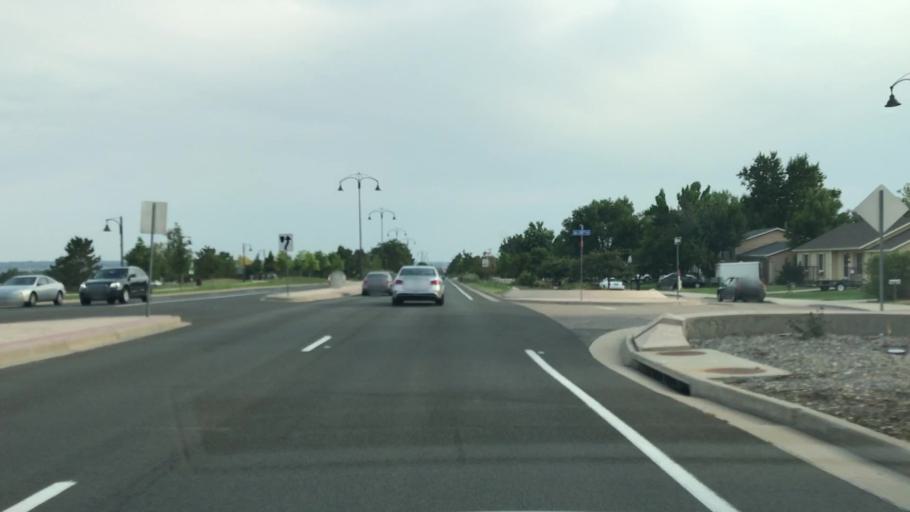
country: US
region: Colorado
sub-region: Broomfield County
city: Broomfield
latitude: 39.9411
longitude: -105.0529
